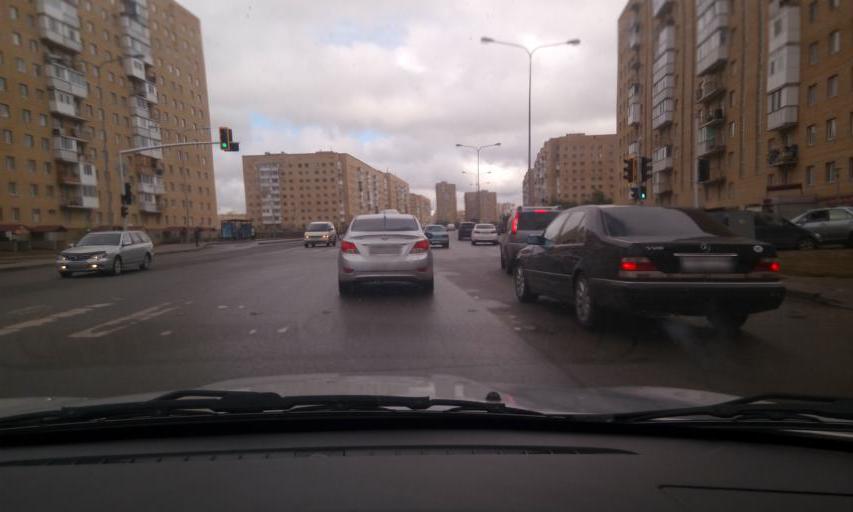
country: KZ
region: Astana Qalasy
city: Astana
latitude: 51.1719
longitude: 71.3798
